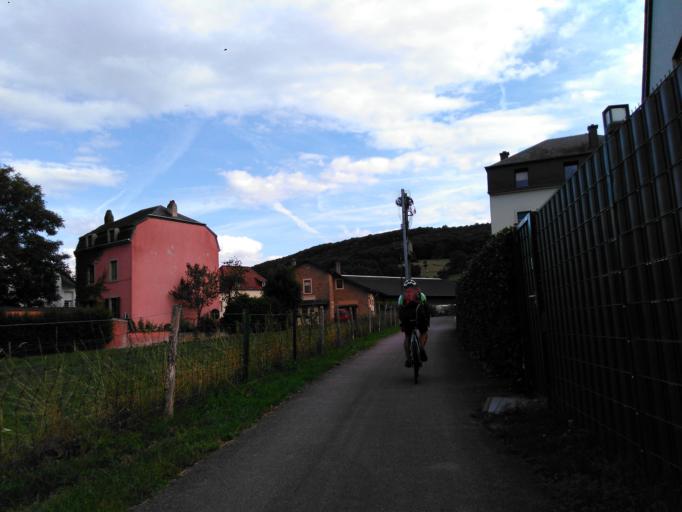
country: DE
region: Rheinland-Pfalz
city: Minden
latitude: 49.8201
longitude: 6.4723
